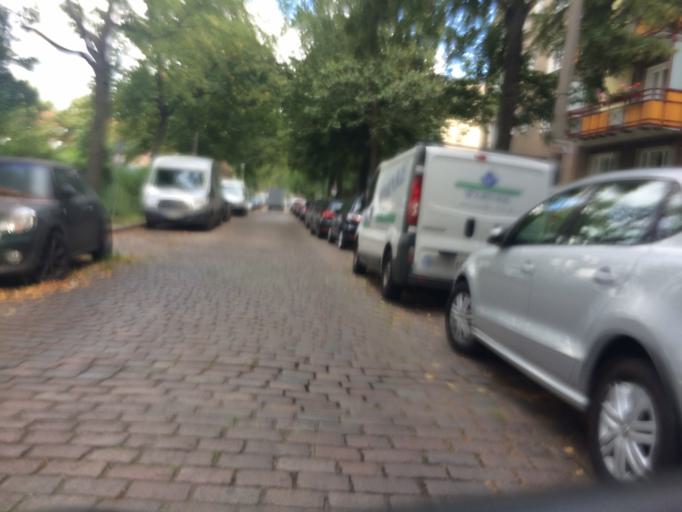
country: DE
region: Berlin
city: Prenzlauer Berg Bezirk
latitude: 52.5544
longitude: 13.4275
